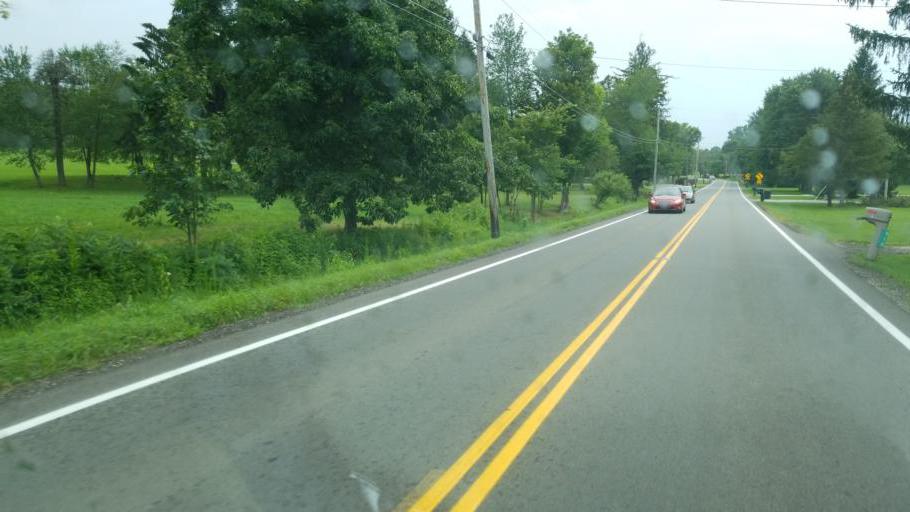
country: US
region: Ohio
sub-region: Richland County
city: Ontario
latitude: 40.7512
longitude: -82.6615
